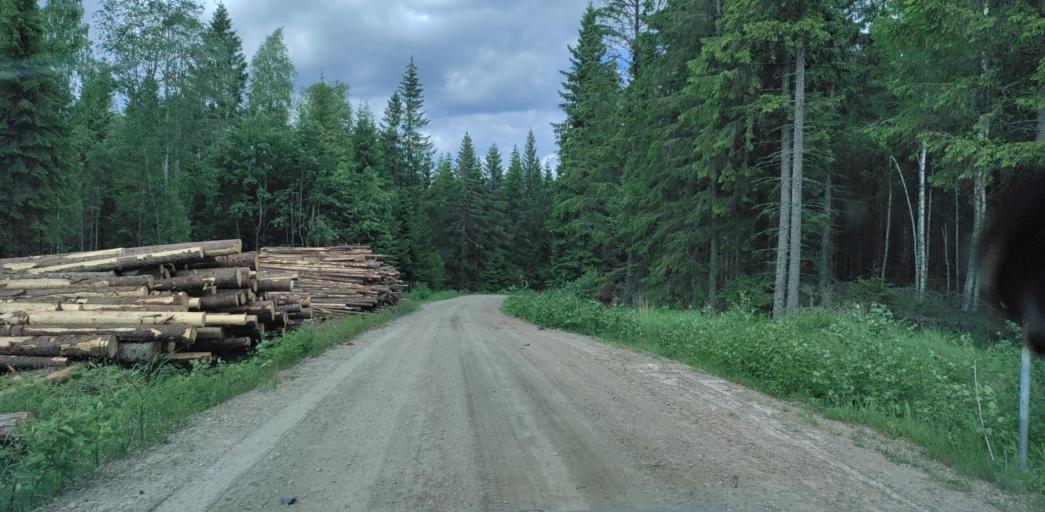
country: SE
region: Vaermland
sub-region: Munkfors Kommun
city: Munkfors
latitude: 59.9600
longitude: 13.4137
